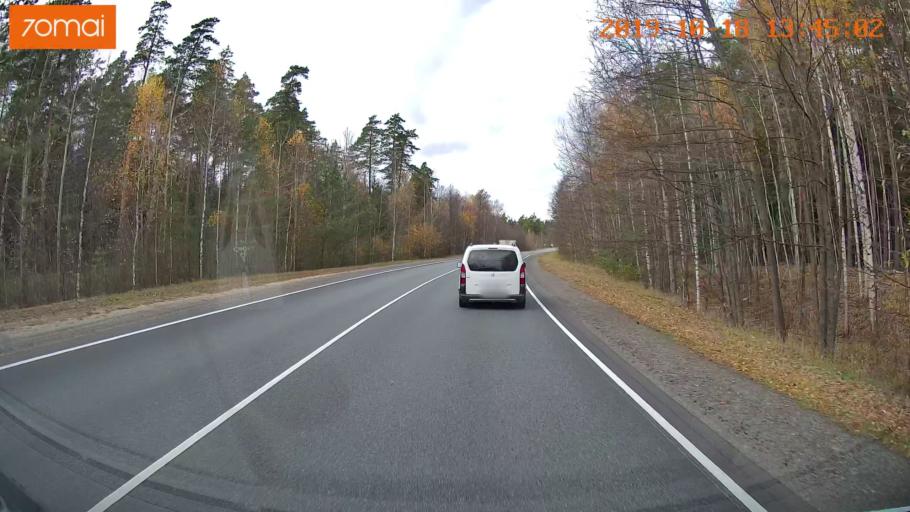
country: RU
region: Rjazan
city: Solotcha
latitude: 54.9414
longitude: 39.9521
